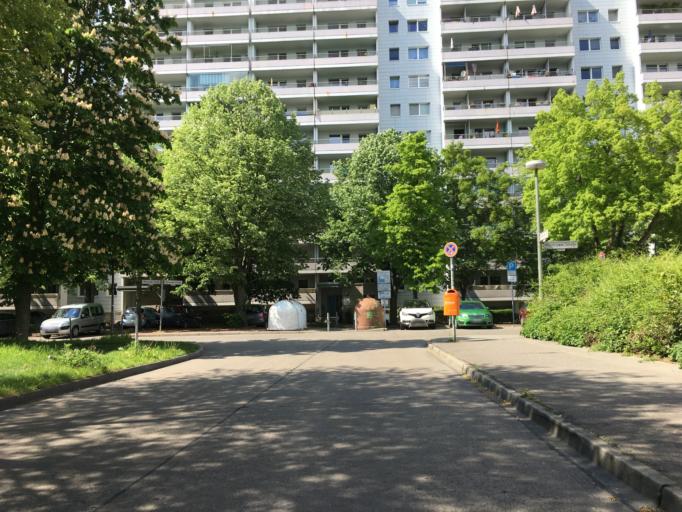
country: DE
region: Berlin
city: Neu-Hohenschoenhausen
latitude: 52.5659
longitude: 13.5074
